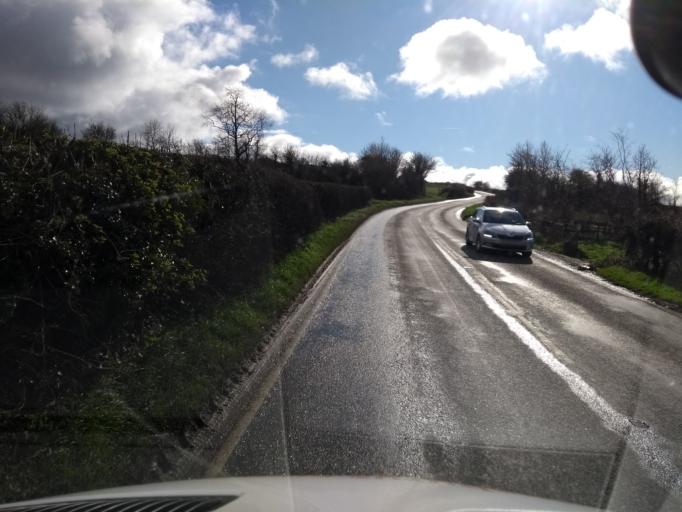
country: GB
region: England
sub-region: Somerset
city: Milborne Port
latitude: 50.9157
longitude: -2.4461
